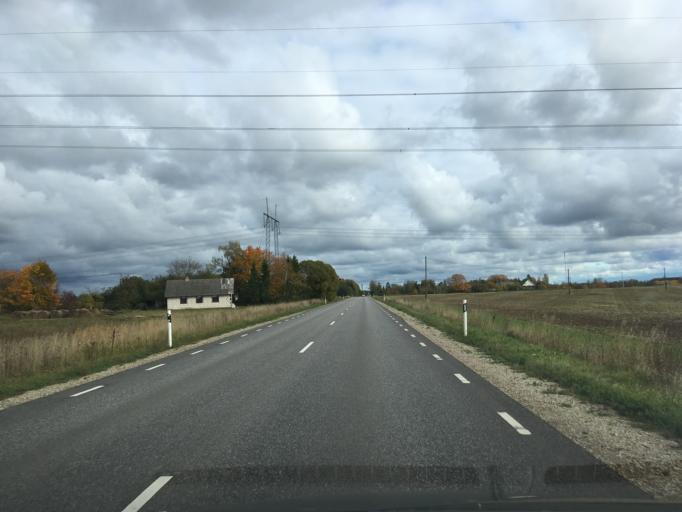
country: EE
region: Harju
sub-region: Anija vald
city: Kehra
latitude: 59.2487
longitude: 25.3099
